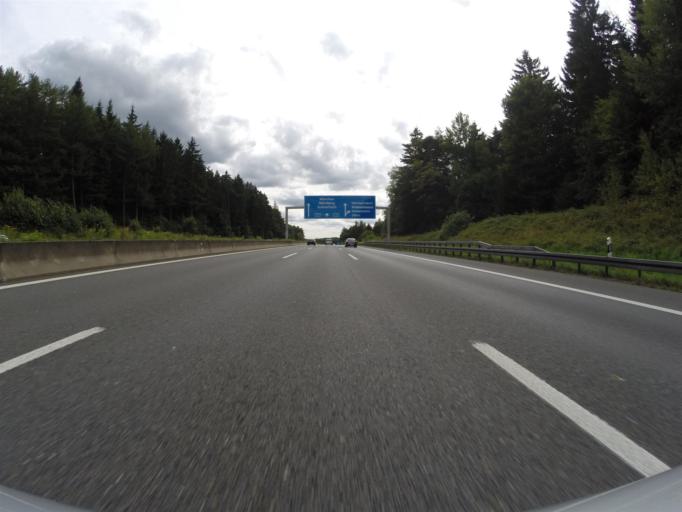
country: DE
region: Bavaria
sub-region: Regierungsbezirk Mittelfranken
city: Kirchensittenbach
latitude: 49.6251
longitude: 11.4137
